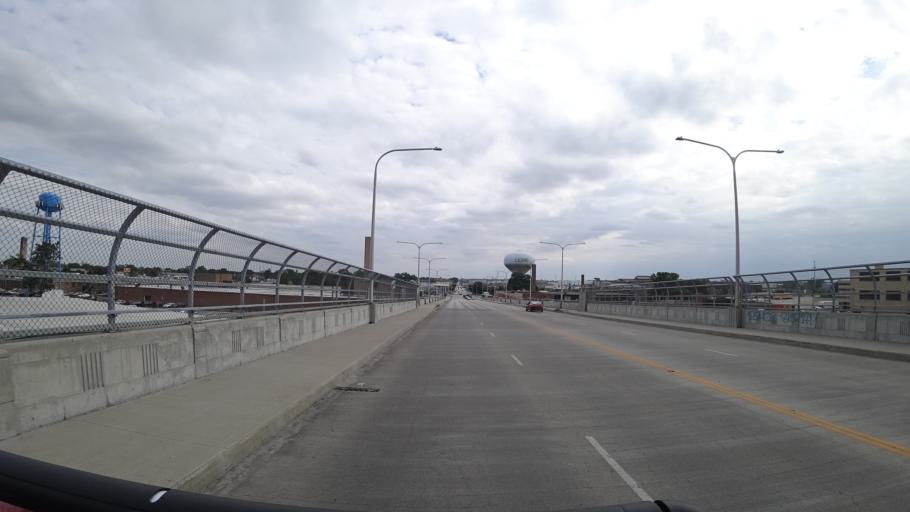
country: US
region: Illinois
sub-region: Cook County
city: Cicero
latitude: 41.8682
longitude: -87.7545
